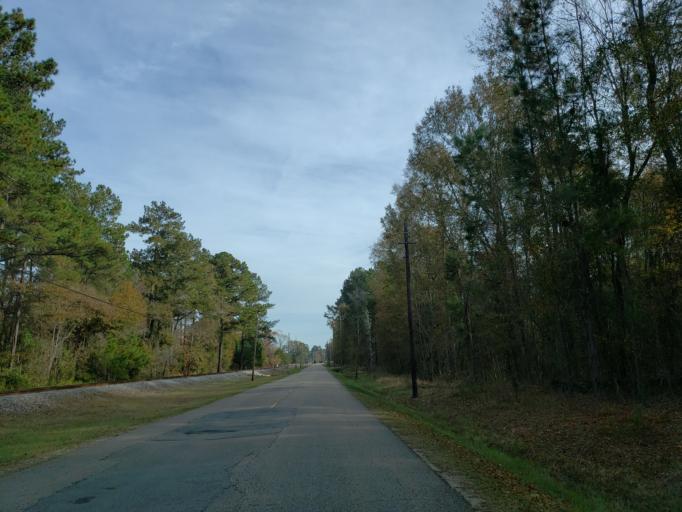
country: US
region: Mississippi
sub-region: Forrest County
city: Glendale
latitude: 31.3529
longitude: -89.3275
